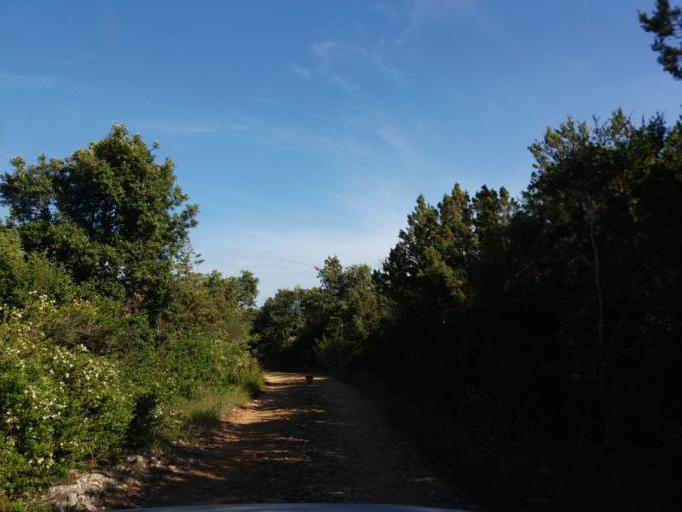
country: HR
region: Zadarska
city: Ugljan
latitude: 44.1317
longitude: 14.8625
